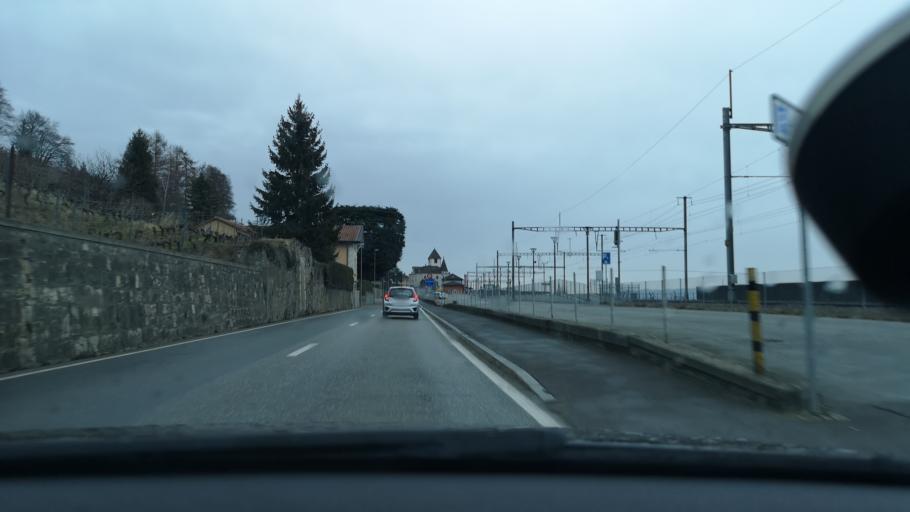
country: CH
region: Vaud
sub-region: Jura-Nord vaudois District
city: Grandson
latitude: 46.8052
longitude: 6.6384
